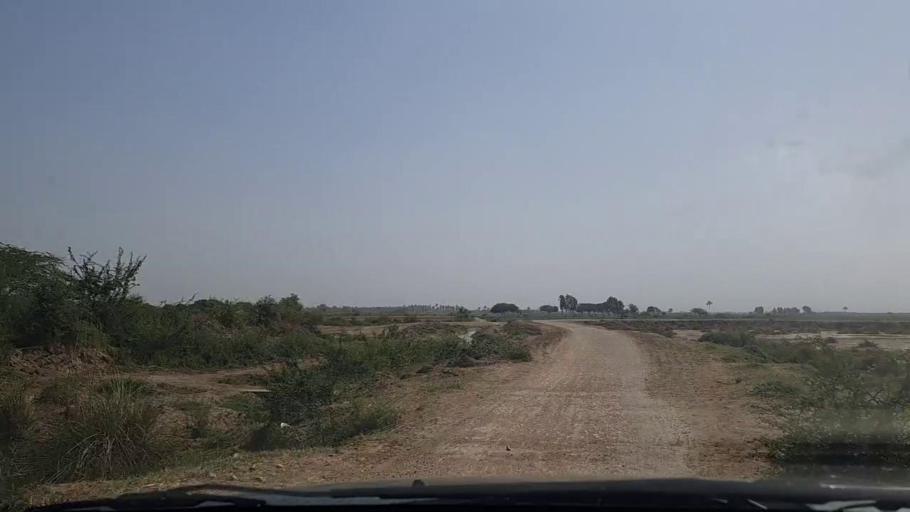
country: PK
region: Sindh
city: Keti Bandar
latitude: 24.2697
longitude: 67.6728
